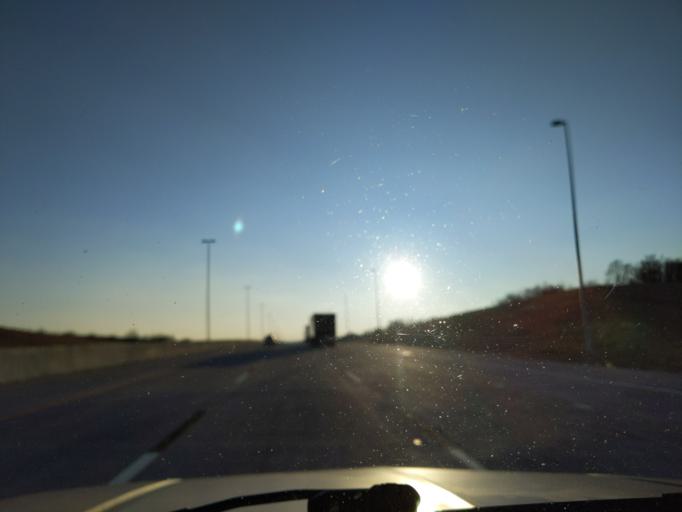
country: US
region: Oklahoma
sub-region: Creek County
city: Kellyville
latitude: 35.9832
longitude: -96.2001
